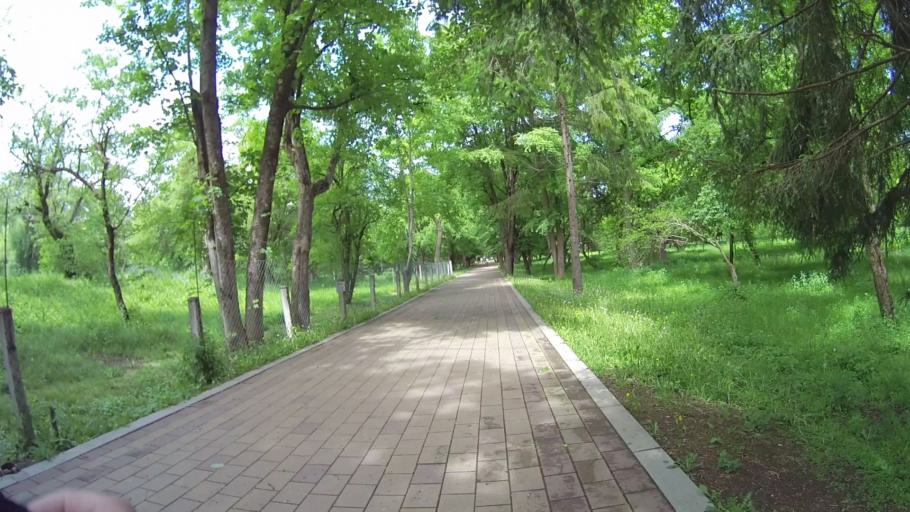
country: RU
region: Kabardino-Balkariya
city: Vol'nyy Aul
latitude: 43.4619
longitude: 43.5886
